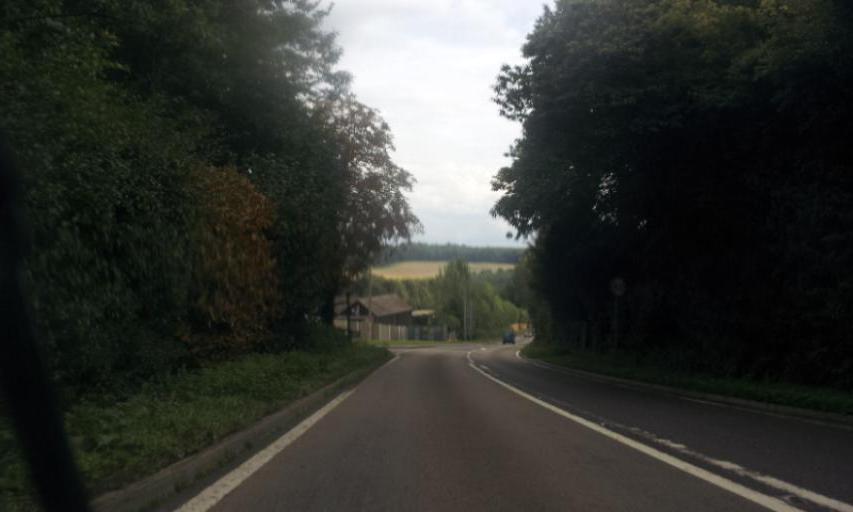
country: GB
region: England
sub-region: Kent
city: Kings Hill
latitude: 51.2622
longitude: 0.3640
